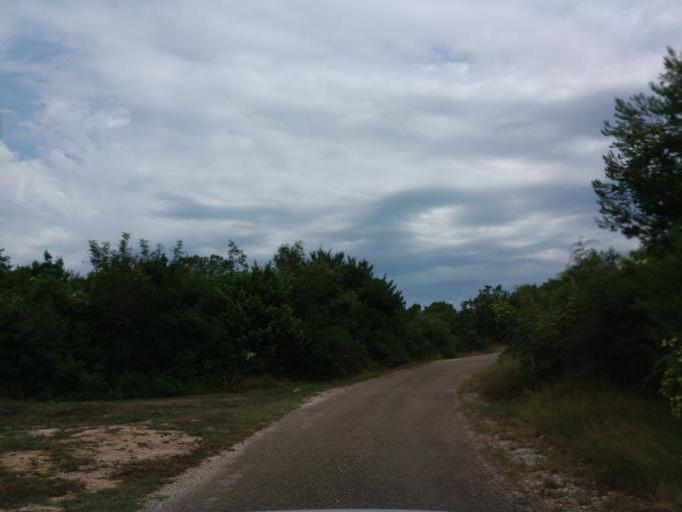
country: HR
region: Zadarska
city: Sali
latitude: 43.9174
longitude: 15.1256
